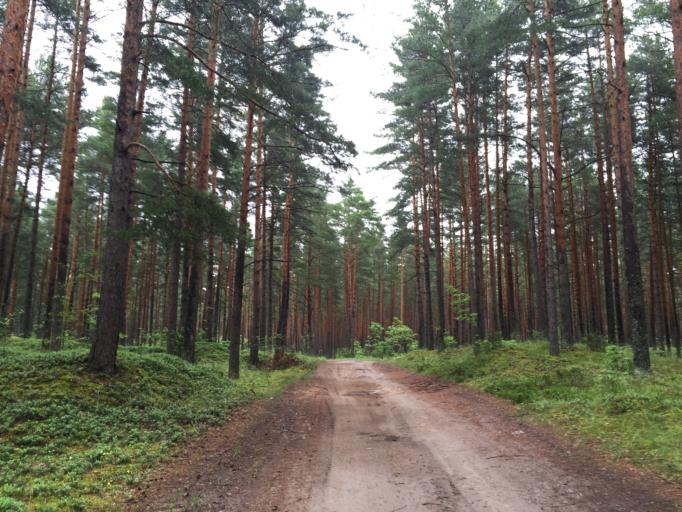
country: LV
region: Riga
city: Jaunciems
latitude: 57.0723
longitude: 24.1475
